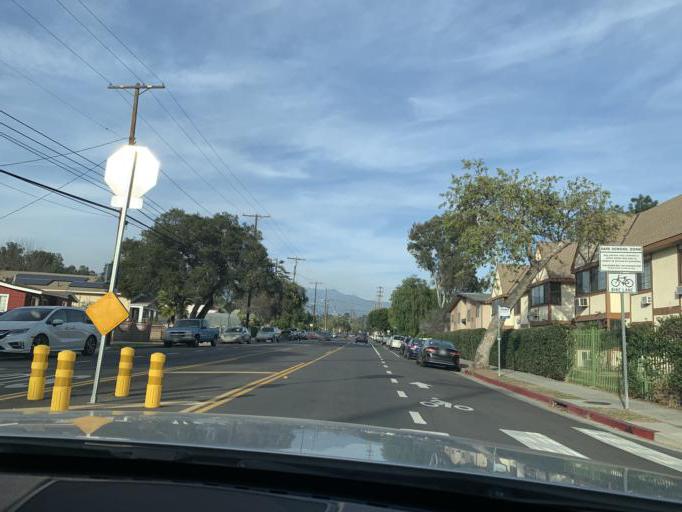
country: US
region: California
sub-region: Los Angeles County
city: South Pasadena
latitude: 34.1163
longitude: -118.1749
